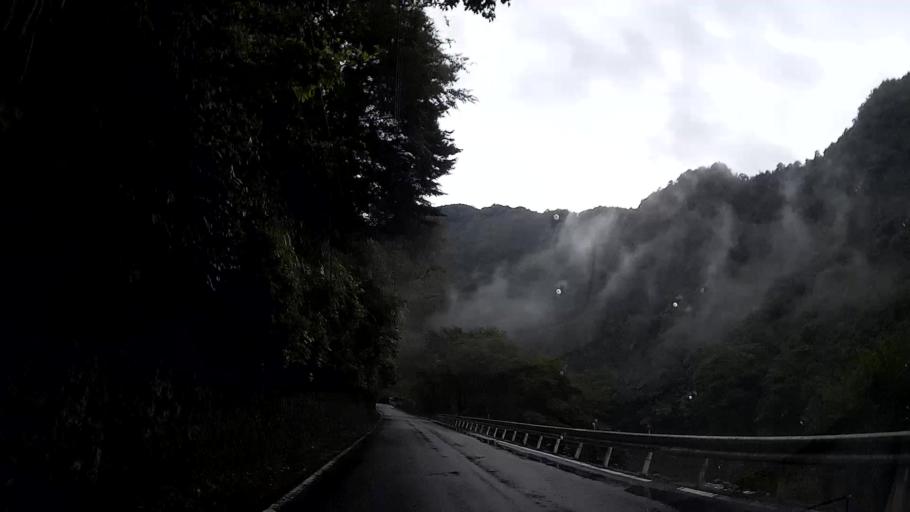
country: JP
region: Oita
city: Hita
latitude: 33.1790
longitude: 131.0131
